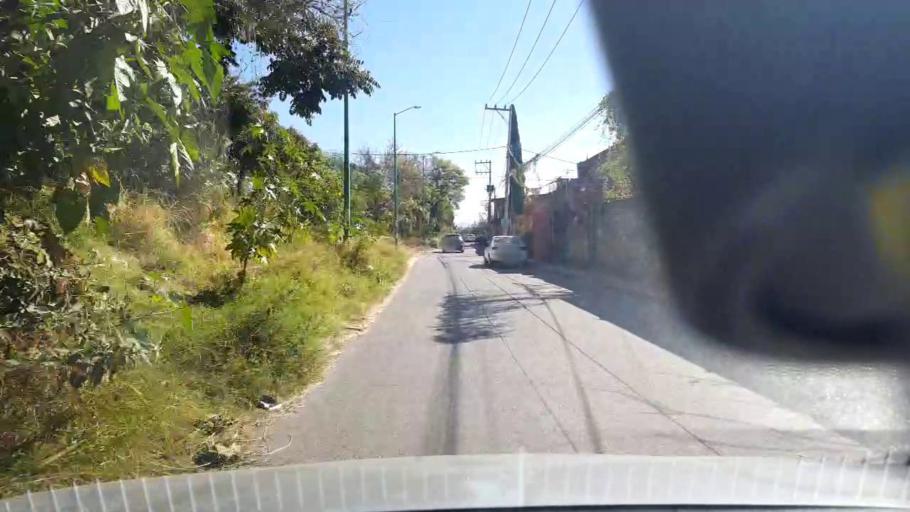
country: MX
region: Morelos
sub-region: Cuernavaca
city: Colonia los Cerritos
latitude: 18.9639
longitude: -99.2240
